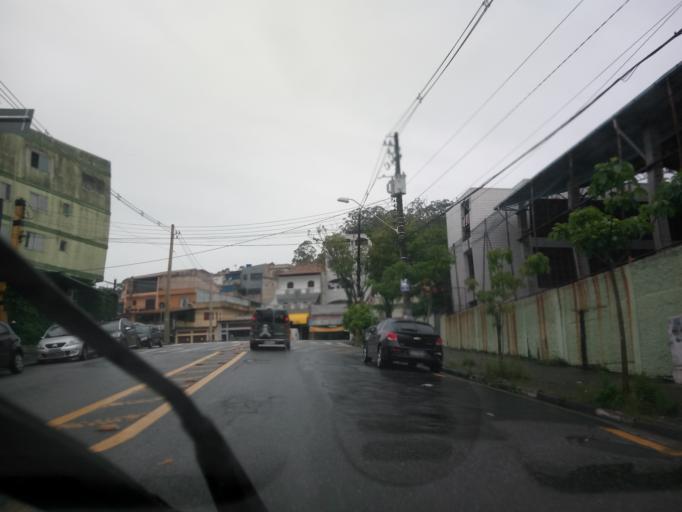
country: BR
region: Sao Paulo
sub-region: Sao Bernardo Do Campo
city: Sao Bernardo do Campo
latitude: -23.7479
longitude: -46.5494
